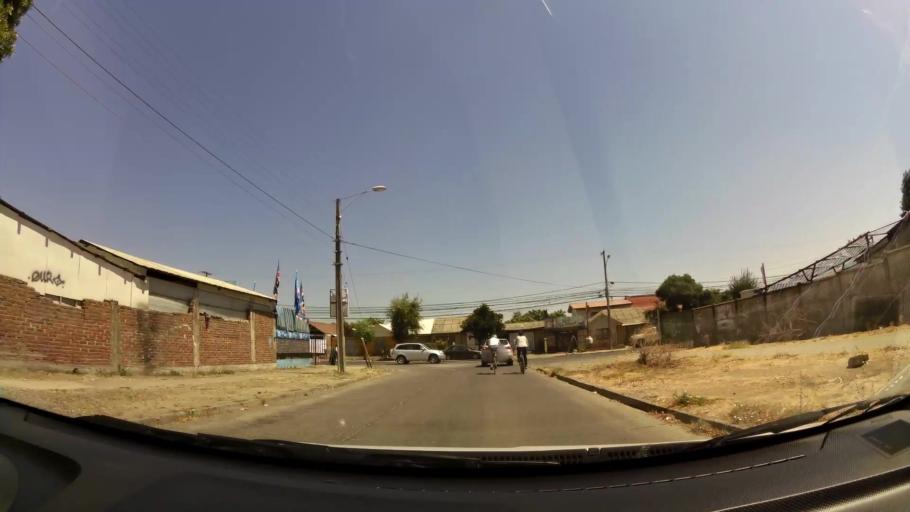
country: CL
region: Maule
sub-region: Provincia de Talca
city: Talca
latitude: -35.4283
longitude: -71.6318
